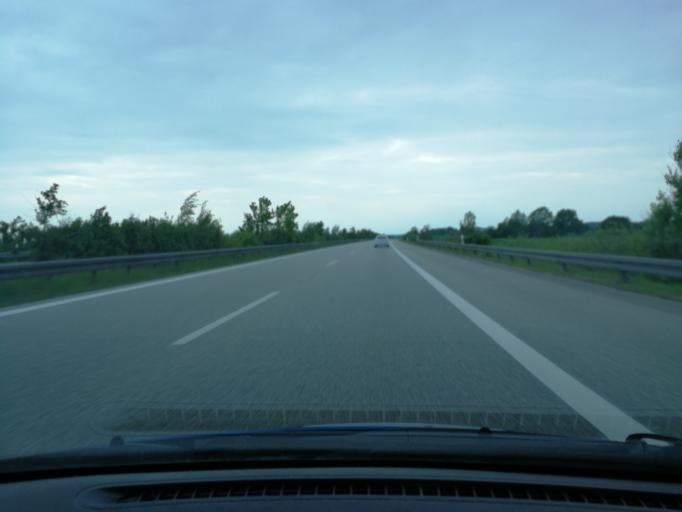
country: DE
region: Mecklenburg-Vorpommern
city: Rehna
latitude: 53.8210
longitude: 11.0872
